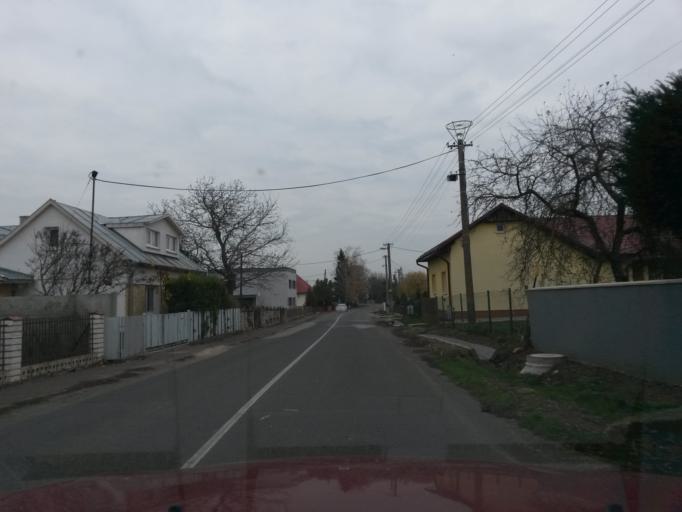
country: SK
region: Kosicky
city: Trebisov
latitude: 48.6360
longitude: 21.6660
